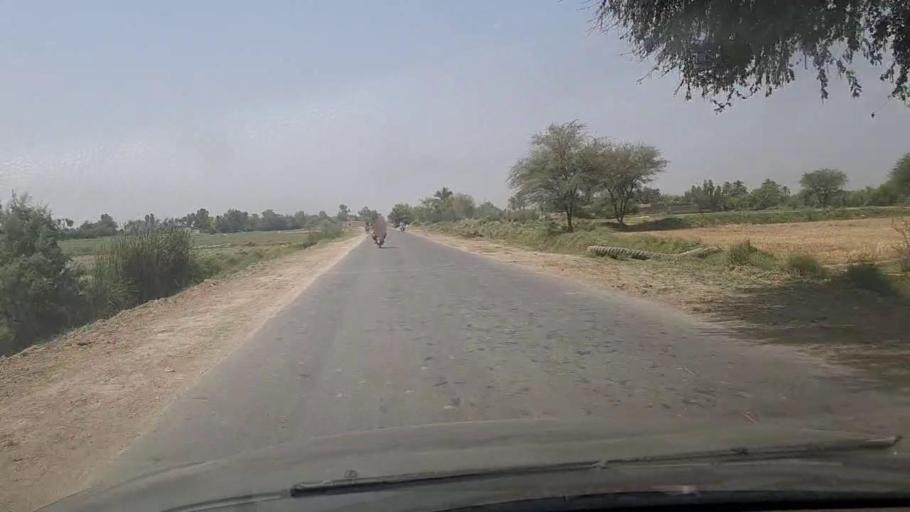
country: PK
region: Sindh
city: Khanpur
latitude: 27.8881
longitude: 69.4786
